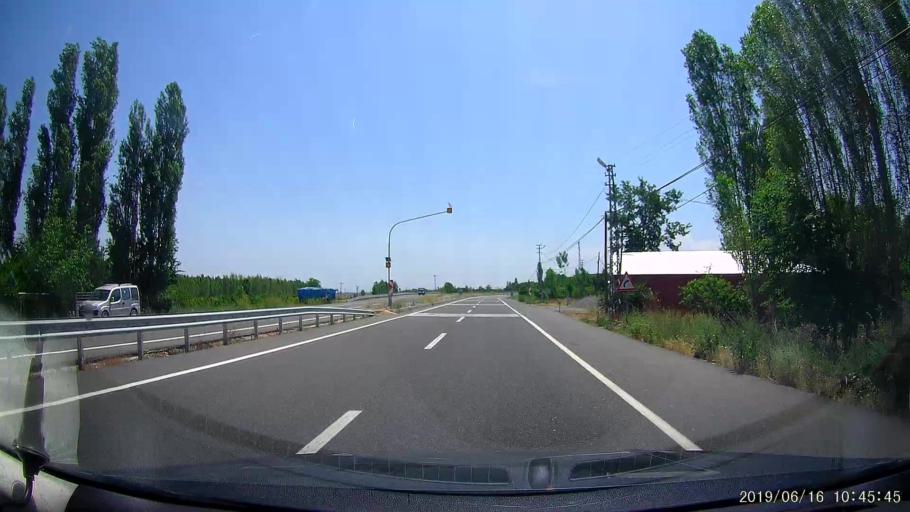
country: AM
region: Armavir
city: Shenavan
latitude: 40.0265
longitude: 43.8730
